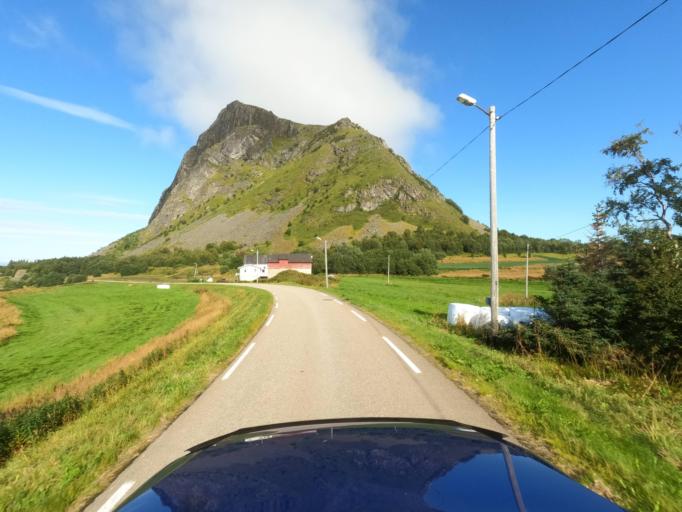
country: NO
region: Nordland
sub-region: Vestvagoy
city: Evjen
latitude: 68.3233
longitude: 14.1086
